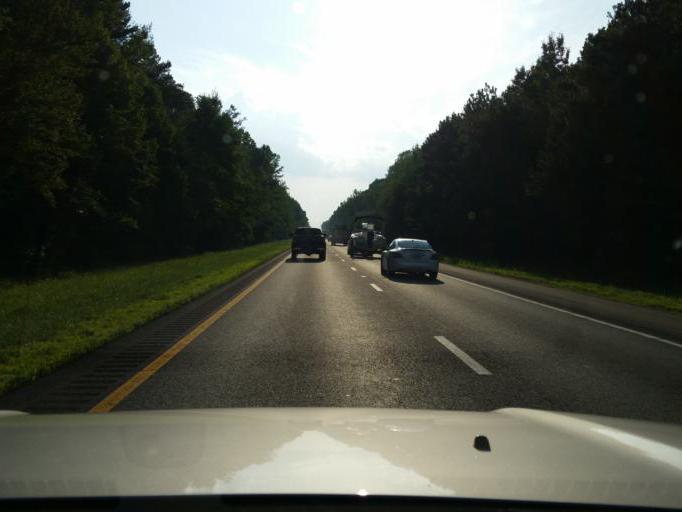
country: US
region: Virginia
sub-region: New Kent County
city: New Kent
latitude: 37.4925
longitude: -76.9989
